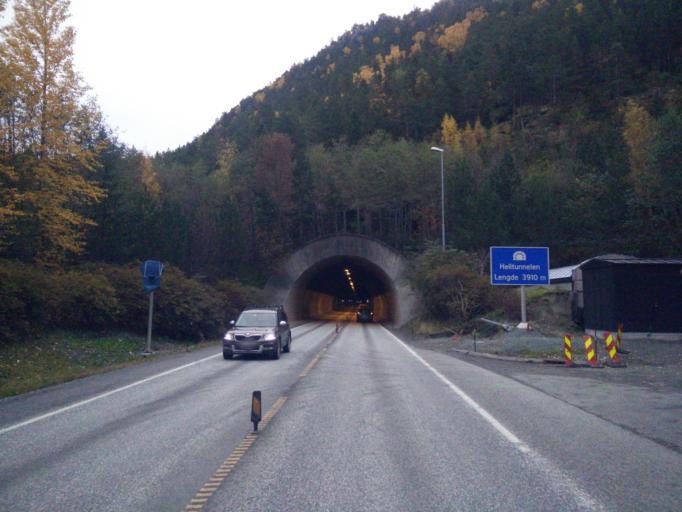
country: NO
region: Sor-Trondelag
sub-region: Malvik
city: Hommelvik
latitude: 63.4165
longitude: 10.8268
